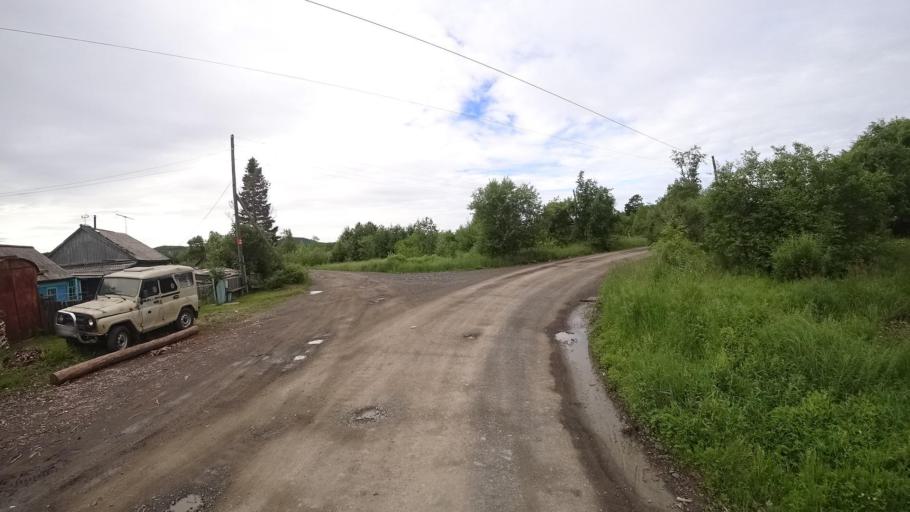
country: RU
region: Khabarovsk Krai
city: Amursk
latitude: 49.9032
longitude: 136.1438
